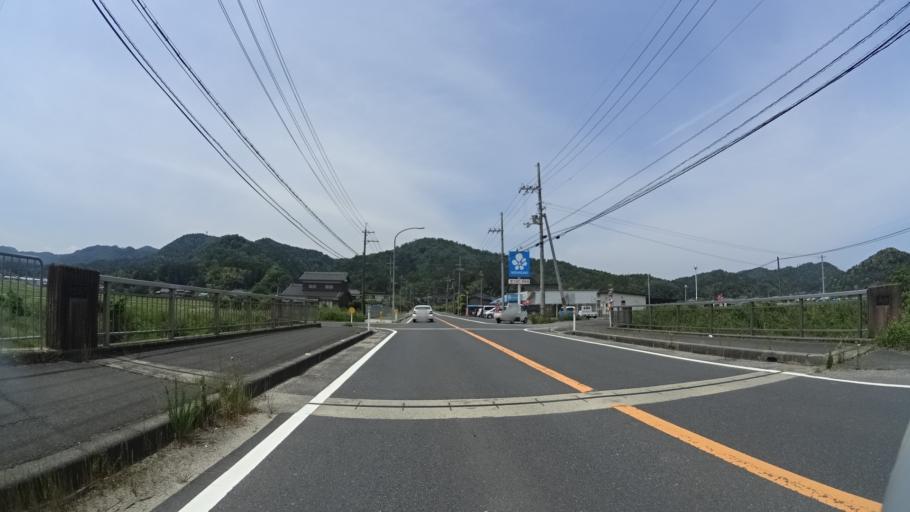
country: JP
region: Hyogo
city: Toyooka
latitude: 35.5887
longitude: 134.9290
